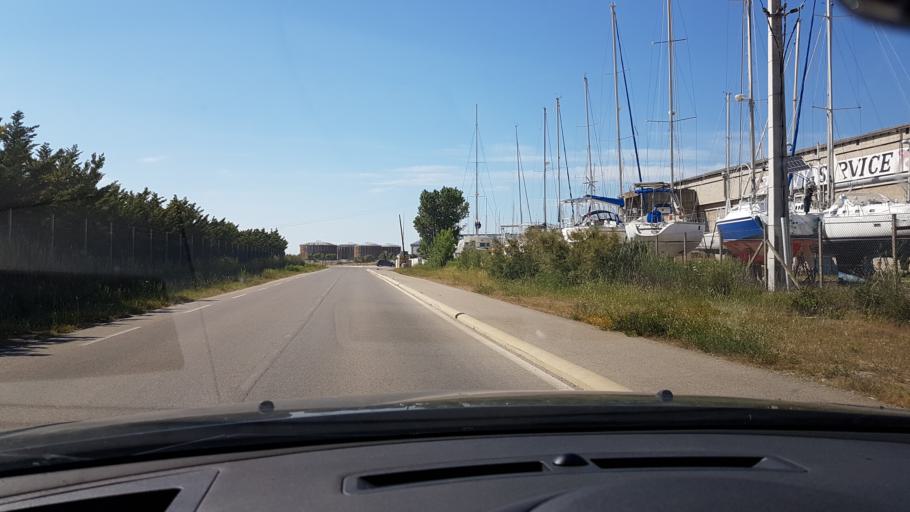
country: FR
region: Provence-Alpes-Cote d'Azur
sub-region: Departement des Bouches-du-Rhone
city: Port-Saint-Louis-du-Rhone
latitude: 43.3840
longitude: 4.8350
